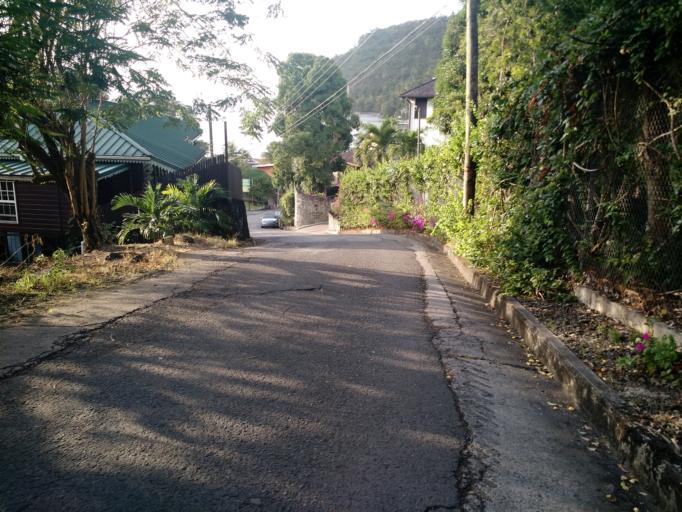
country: LC
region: Anse-la-Raye
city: Anse La Raye
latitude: 13.9641
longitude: -61.0237
